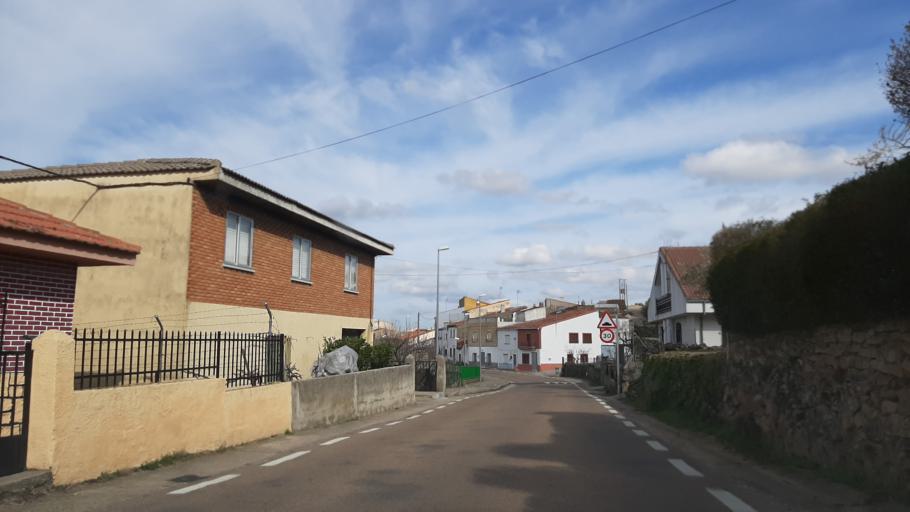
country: ES
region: Castille and Leon
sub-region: Provincia de Salamanca
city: Villarino de los Aires
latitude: 41.2653
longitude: -6.4690
